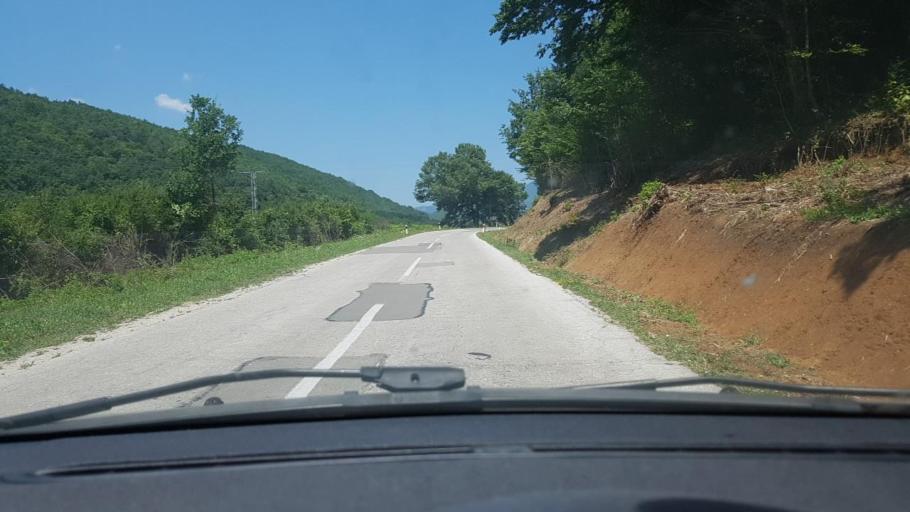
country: BA
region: Federation of Bosnia and Herzegovina
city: Orasac
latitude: 44.5776
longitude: 16.0766
